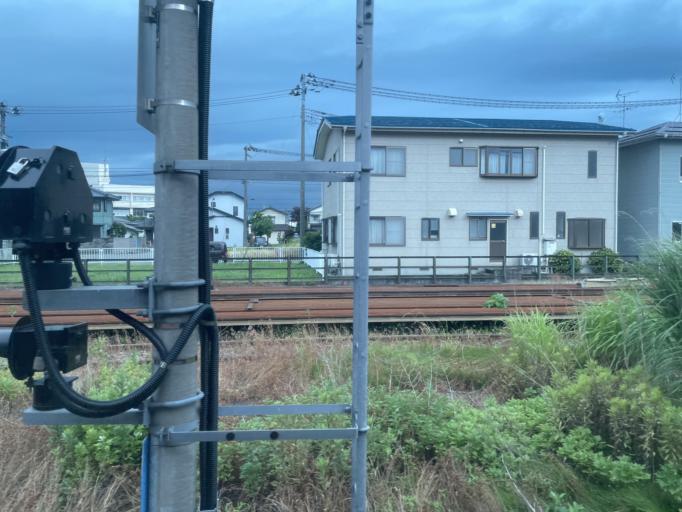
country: JP
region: Niigata
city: Yoshida-kasugacho
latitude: 37.6866
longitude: 138.8783
